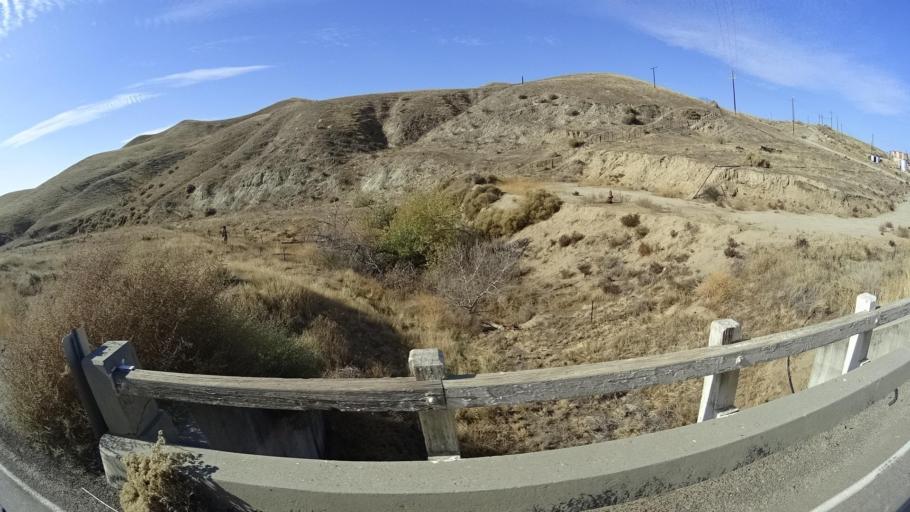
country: US
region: California
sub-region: Kern County
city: Oildale
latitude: 35.5378
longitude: -118.9594
